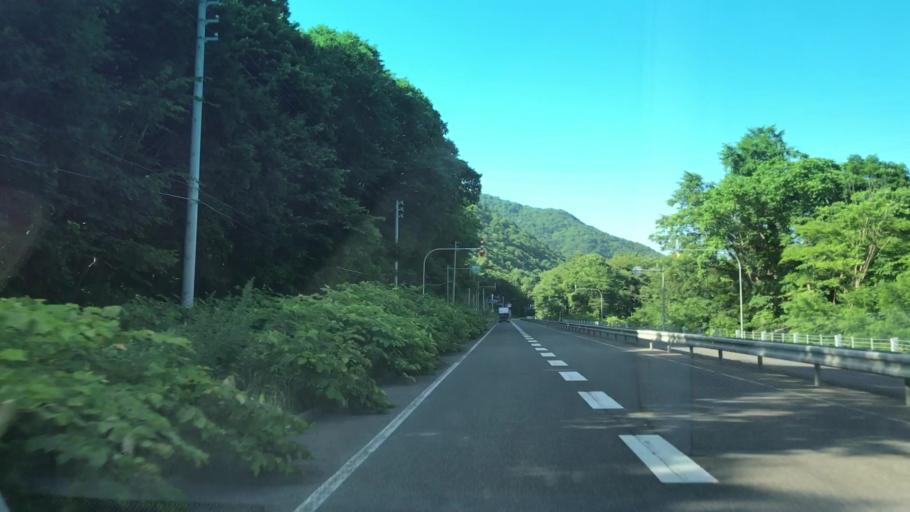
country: JP
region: Hokkaido
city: Iwanai
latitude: 43.0142
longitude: 140.6661
